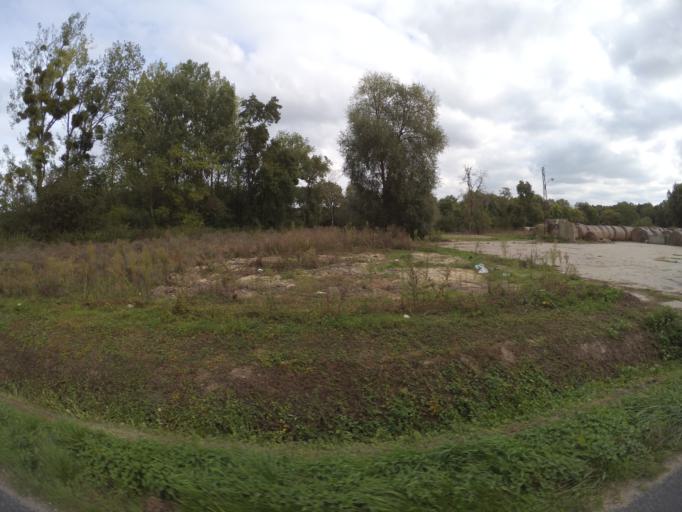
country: FR
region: Centre
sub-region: Departement d'Indre-et-Loire
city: Reugny
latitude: 47.4674
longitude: 0.8795
